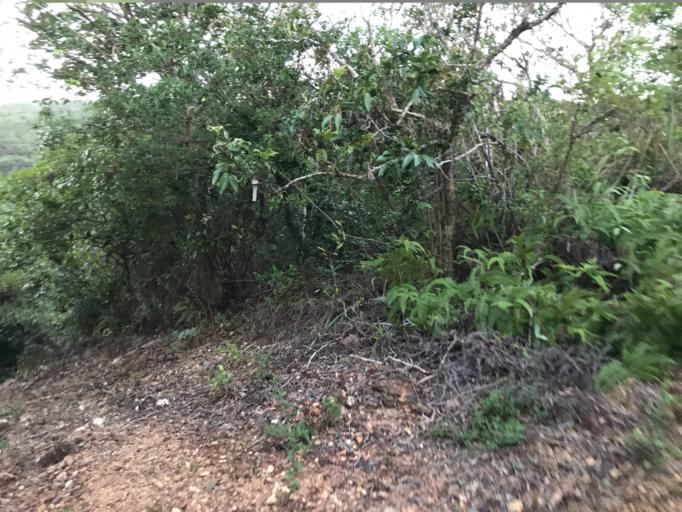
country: HK
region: Tai Po
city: Tai Po
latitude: 22.4715
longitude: 114.1455
